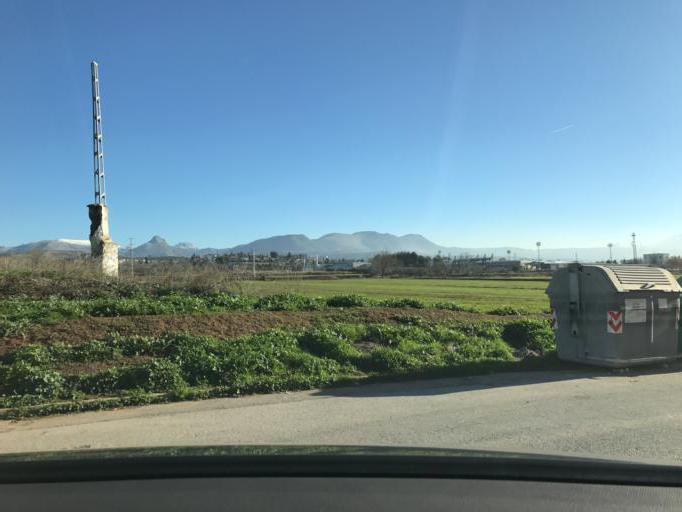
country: ES
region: Andalusia
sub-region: Provincia de Granada
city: Albolote
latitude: 37.2359
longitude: -3.6563
